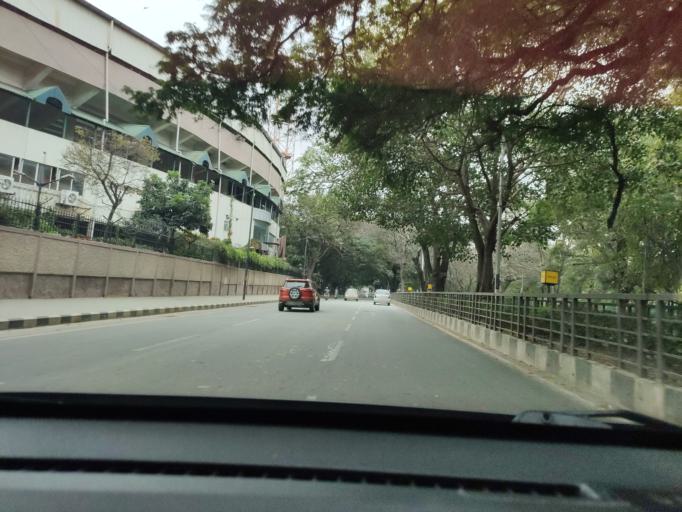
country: IN
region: Karnataka
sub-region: Bangalore Urban
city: Bangalore
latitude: 12.9790
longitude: 77.5982
